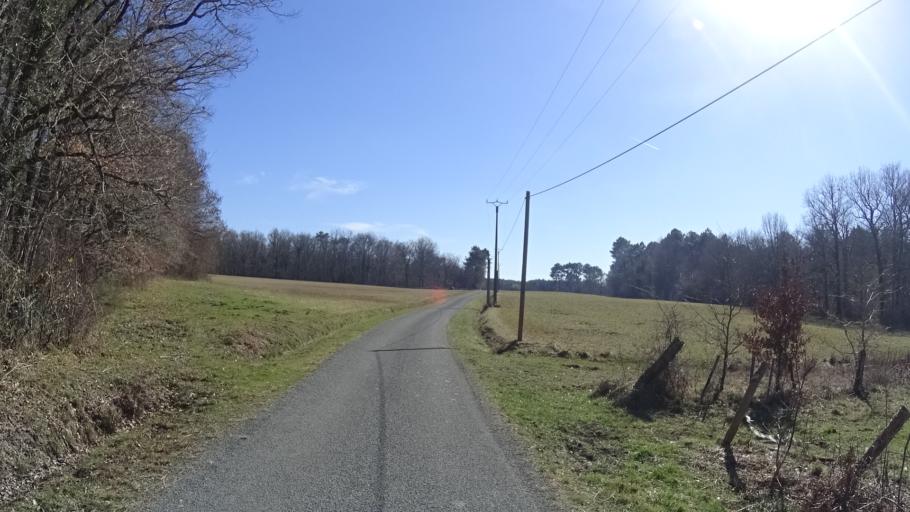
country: FR
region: Aquitaine
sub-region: Departement de la Dordogne
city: Saint-Aulaye
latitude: 45.1400
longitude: 0.2088
